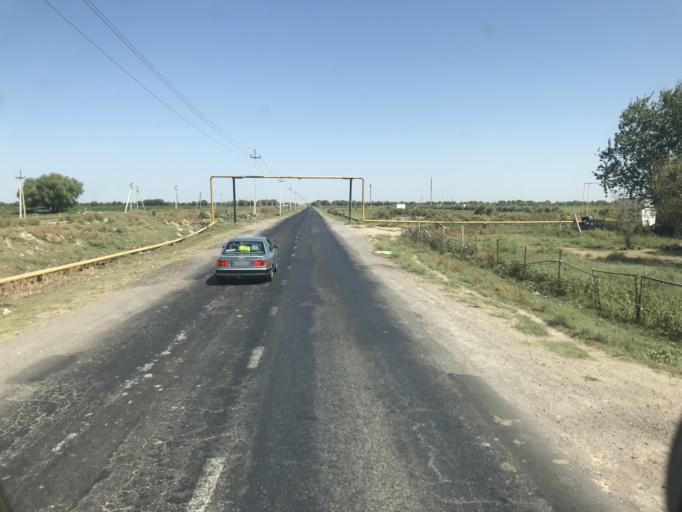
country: KZ
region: Ongtustik Qazaqstan
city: Ilyich
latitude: 40.9017
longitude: 68.4882
